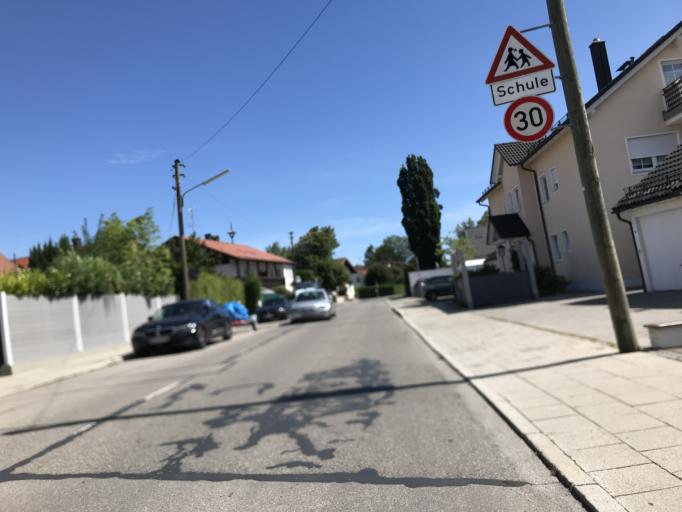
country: DE
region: Bavaria
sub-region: Upper Bavaria
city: Grobenzell
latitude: 48.1790
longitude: 11.3594
